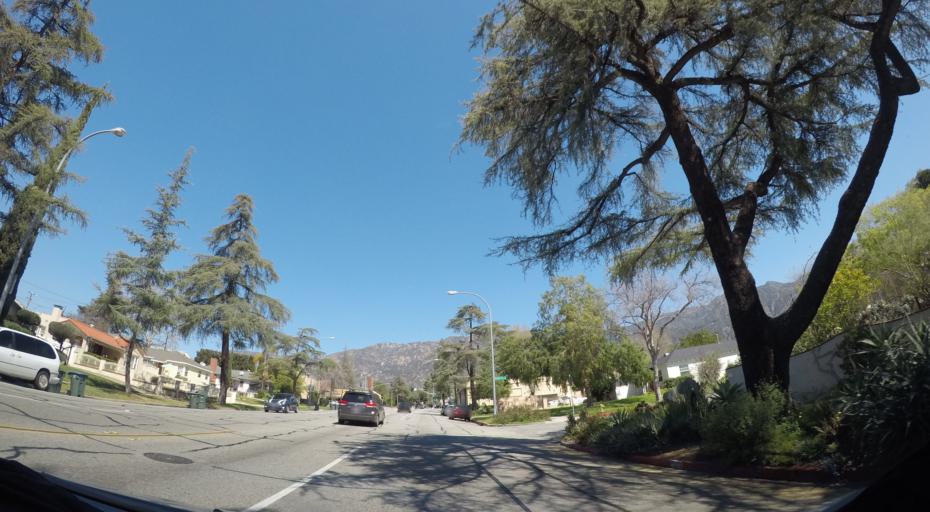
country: US
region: California
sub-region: Los Angeles County
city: Altadena
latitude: 34.1679
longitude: -118.1130
